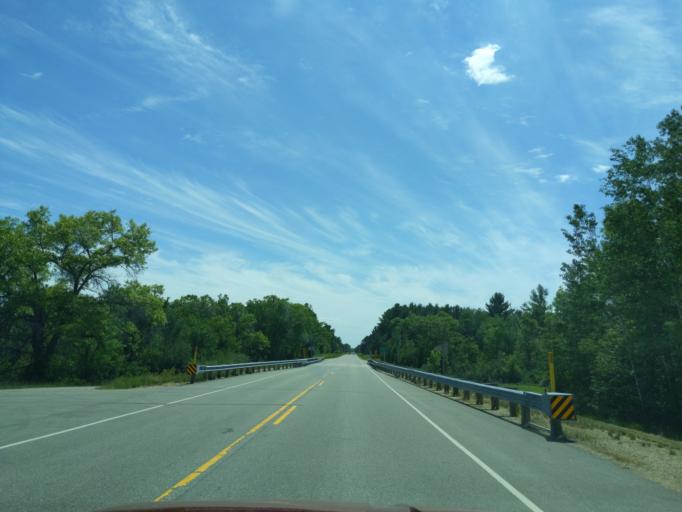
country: US
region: Wisconsin
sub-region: Marquette County
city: Montello
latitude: 43.9166
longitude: -89.3122
